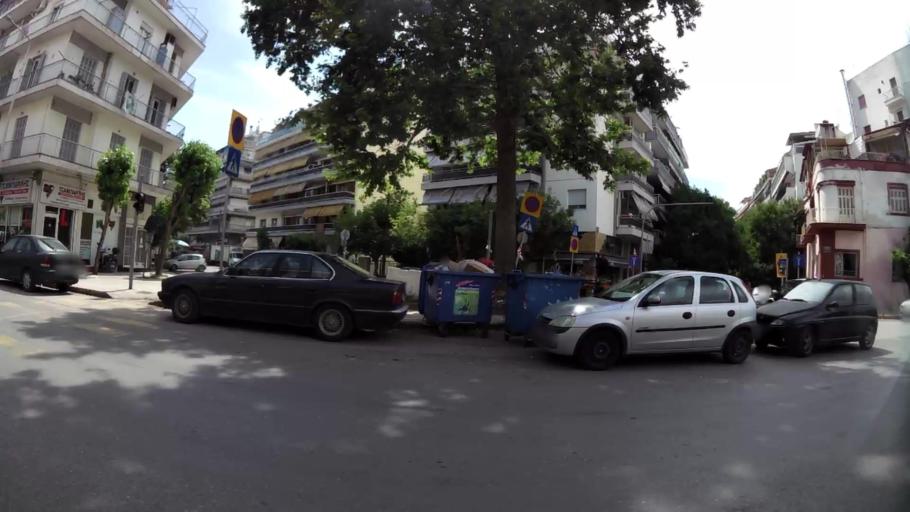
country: GR
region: Central Macedonia
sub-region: Nomos Thessalonikis
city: Kalamaria
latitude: 40.6001
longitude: 22.9595
